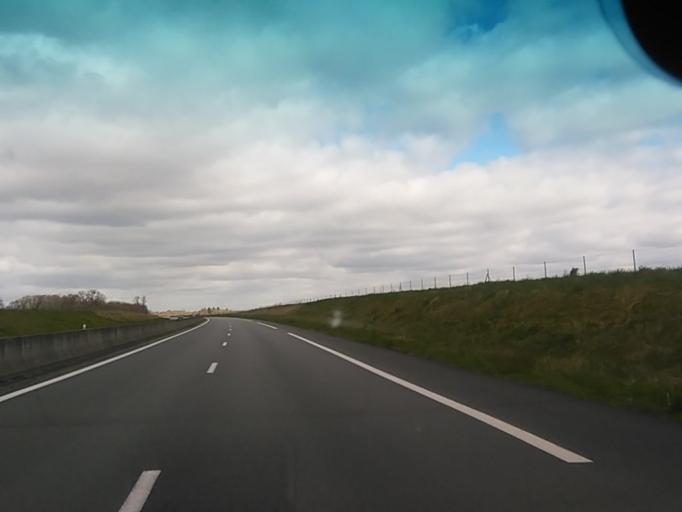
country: FR
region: Haute-Normandie
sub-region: Departement de l'Eure
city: Bernay
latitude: 49.1227
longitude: 0.5309
